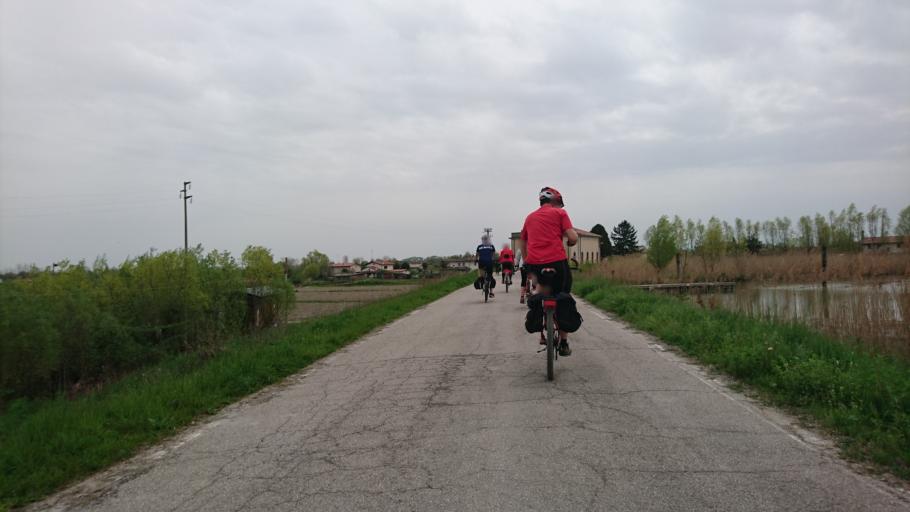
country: IT
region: Veneto
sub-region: Provincia di Venezia
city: Concordia Sagittaria
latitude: 45.7029
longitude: 12.8712
